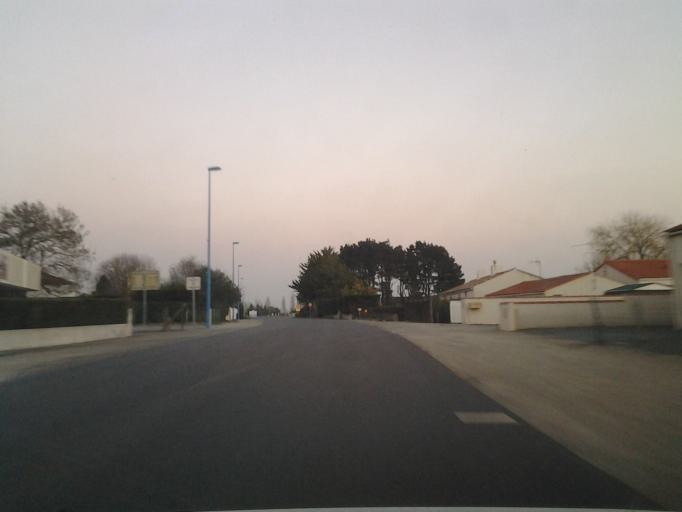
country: FR
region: Pays de la Loire
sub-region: Departement de la Vendee
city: Beauvoir-sur-Mer
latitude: 46.9066
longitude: -2.0258
